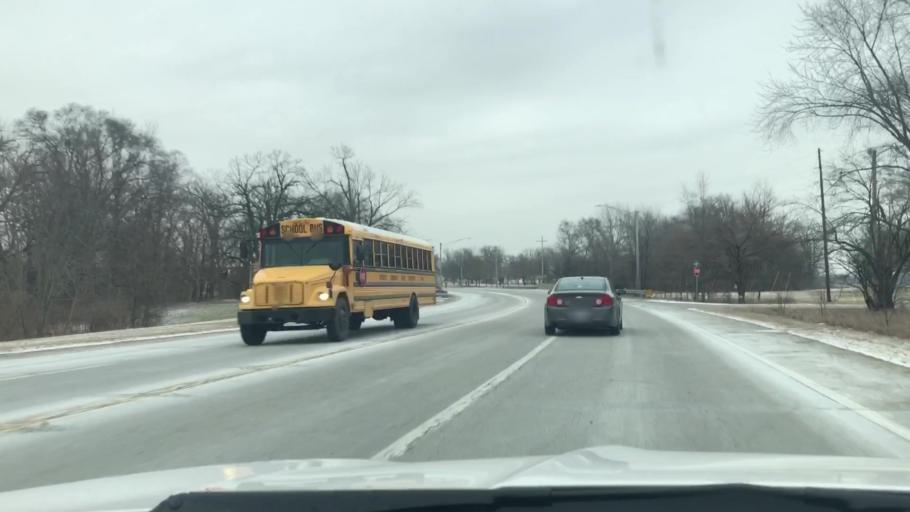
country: US
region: Indiana
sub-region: Fulton County
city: Rochester
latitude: 41.0620
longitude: -86.1987
